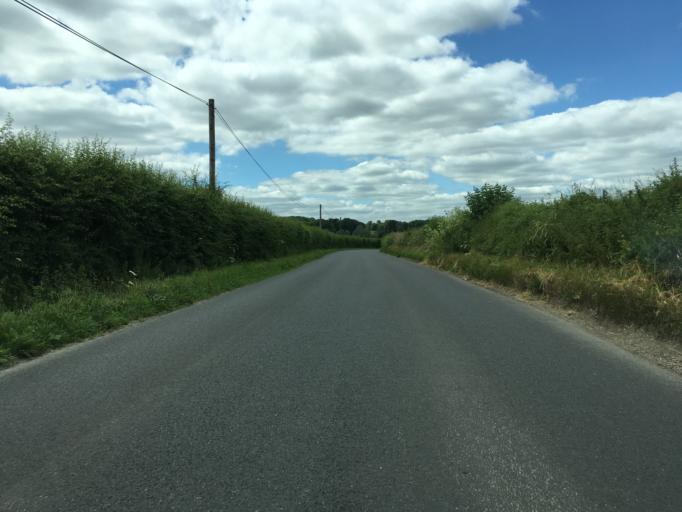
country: GB
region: England
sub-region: Hampshire
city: Highclere
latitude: 51.2387
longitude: -1.3779
